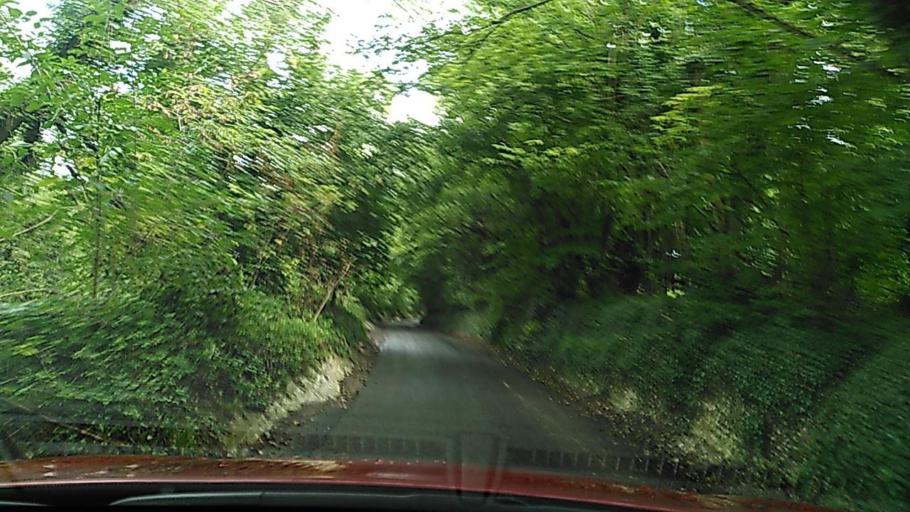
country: GB
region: England
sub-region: Oxfordshire
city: Henley on Thames
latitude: 51.5189
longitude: -0.9168
